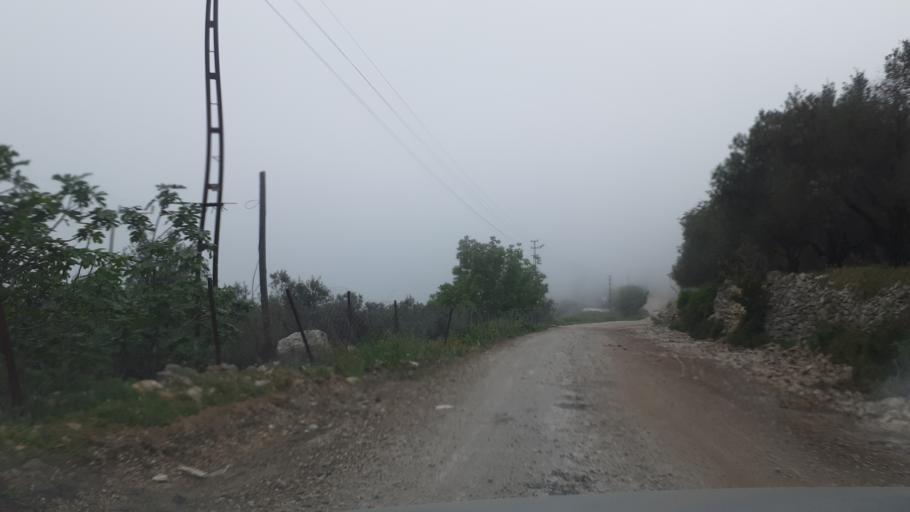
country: TR
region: Hatay
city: Yeditepe
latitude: 35.9693
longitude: 36.0053
